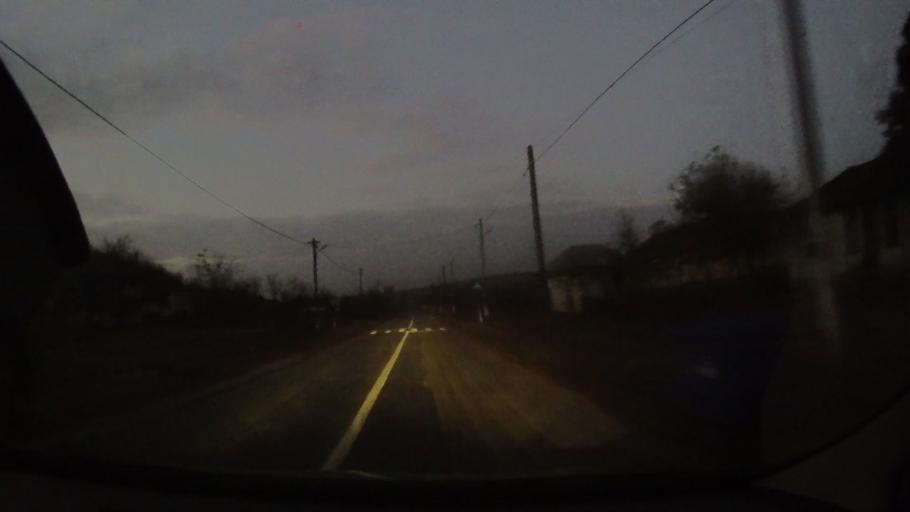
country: RO
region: Constanta
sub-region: Comuna Ion Corvin
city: Ion Corvin
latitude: 44.1435
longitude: 27.8333
